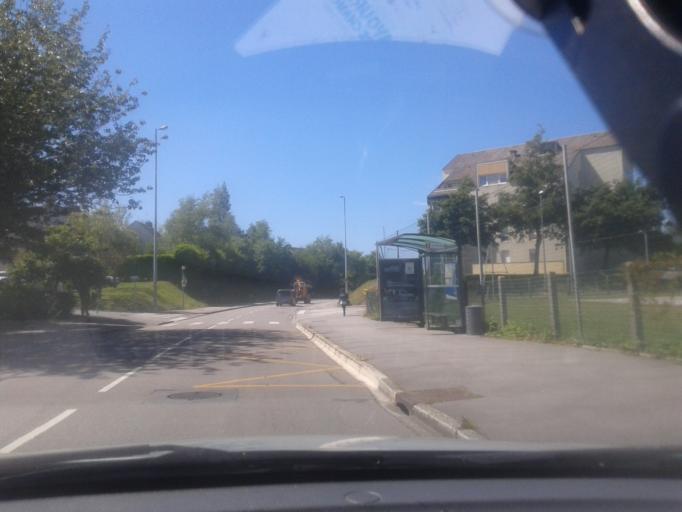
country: FR
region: Lower Normandy
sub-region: Departement de la Manche
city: Octeville
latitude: 49.6312
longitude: -1.6461
